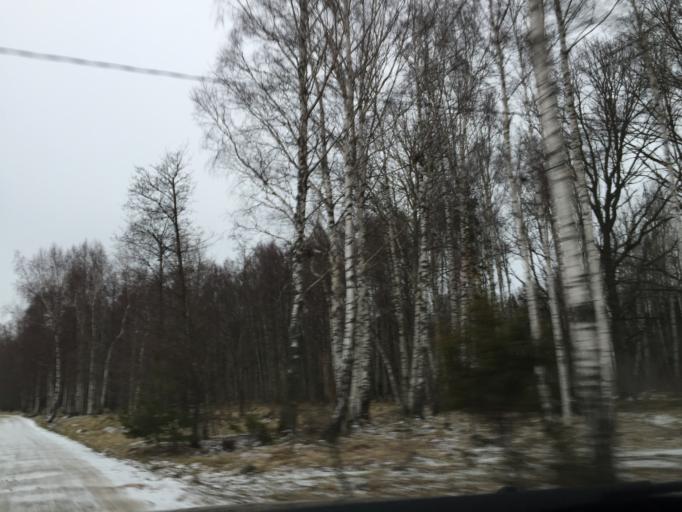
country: LV
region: Saulkrastu
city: Saulkrasti
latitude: 57.5032
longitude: 24.3829
